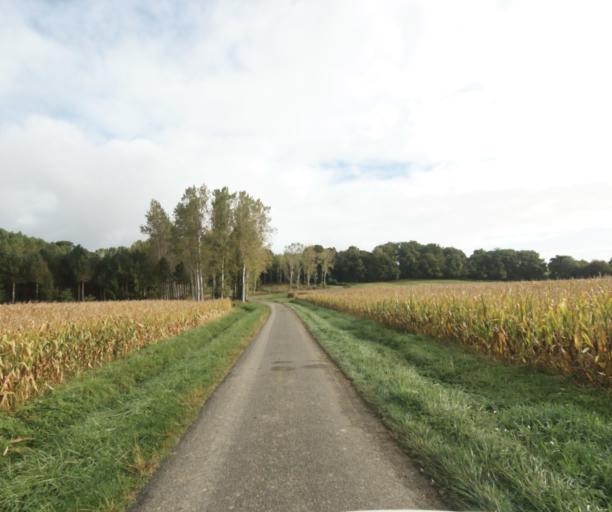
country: FR
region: Midi-Pyrenees
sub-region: Departement du Gers
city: Nogaro
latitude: 43.8084
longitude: -0.0657
